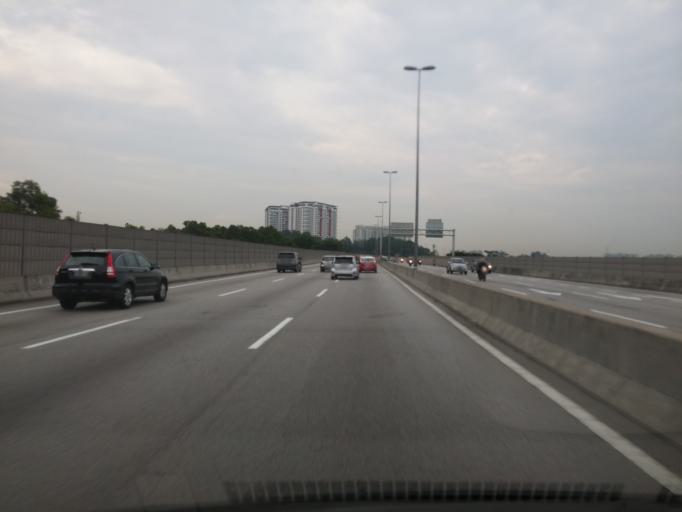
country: MY
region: Selangor
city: Kampong Baharu Balakong
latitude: 3.0674
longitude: 101.6846
